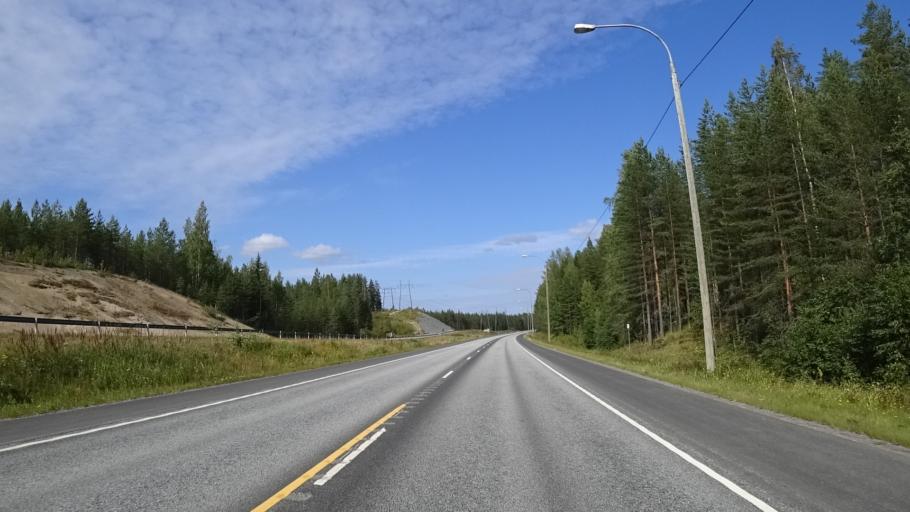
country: FI
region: North Karelia
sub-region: Joensuu
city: Joensuu
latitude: 62.6815
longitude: 29.7962
